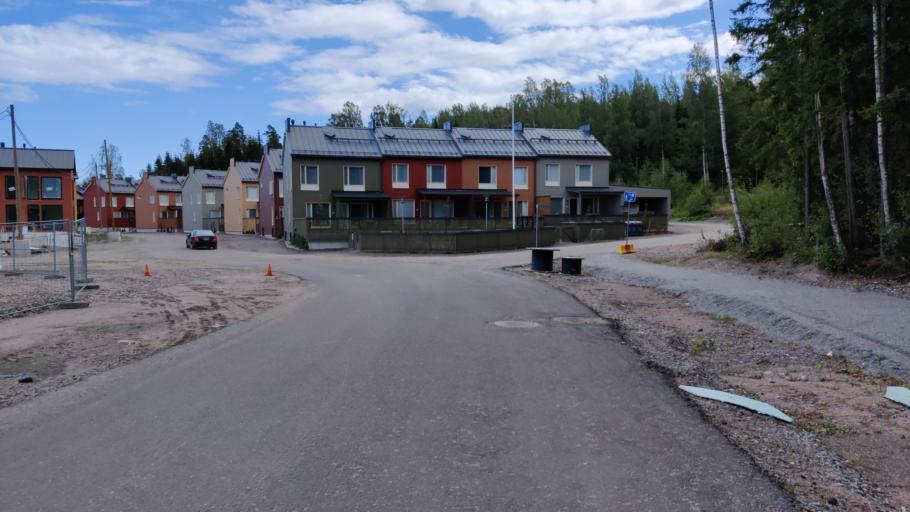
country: FI
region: Uusimaa
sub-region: Helsinki
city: Teekkarikylae
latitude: 60.2555
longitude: 24.8405
